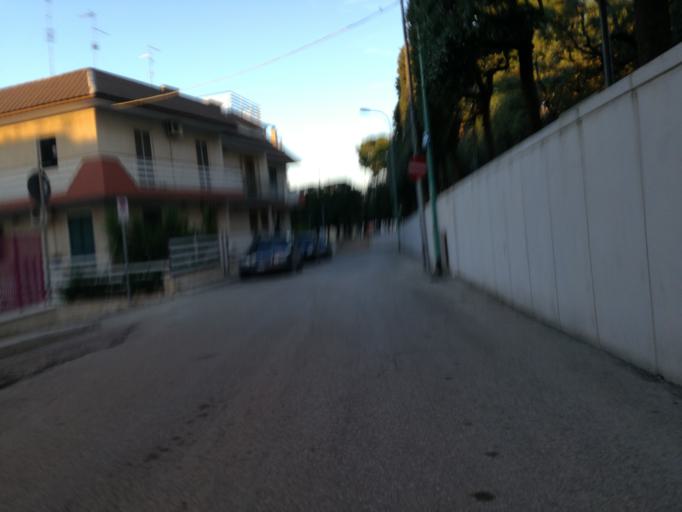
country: IT
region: Apulia
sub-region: Provincia di Bari
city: Adelfia
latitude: 41.0012
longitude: 16.8755
